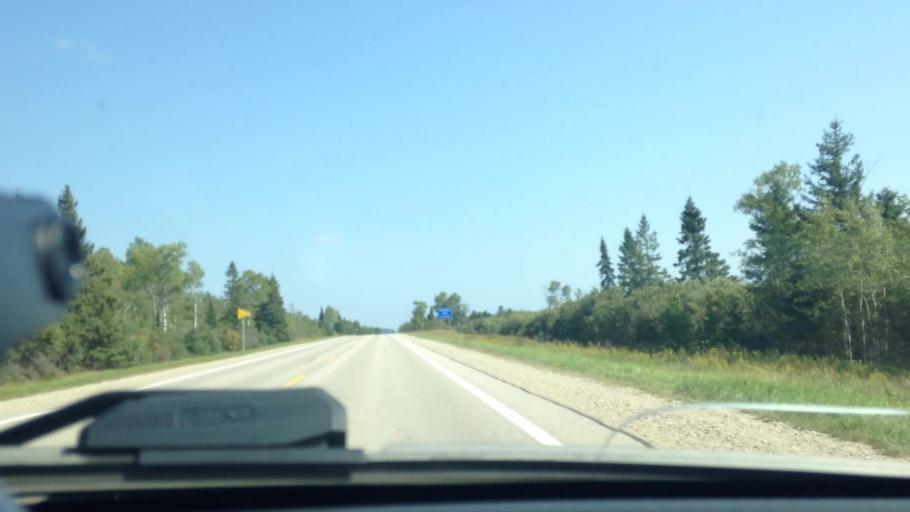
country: US
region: Michigan
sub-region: Luce County
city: Newberry
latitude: 46.3104
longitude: -85.6027
